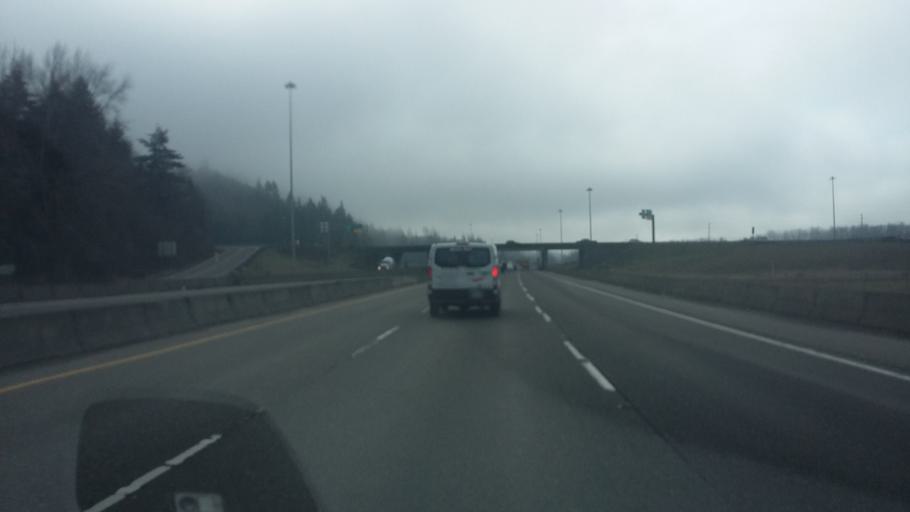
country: US
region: Washington
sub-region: Cowlitz County
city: Kelso
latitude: 46.1089
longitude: -122.8805
